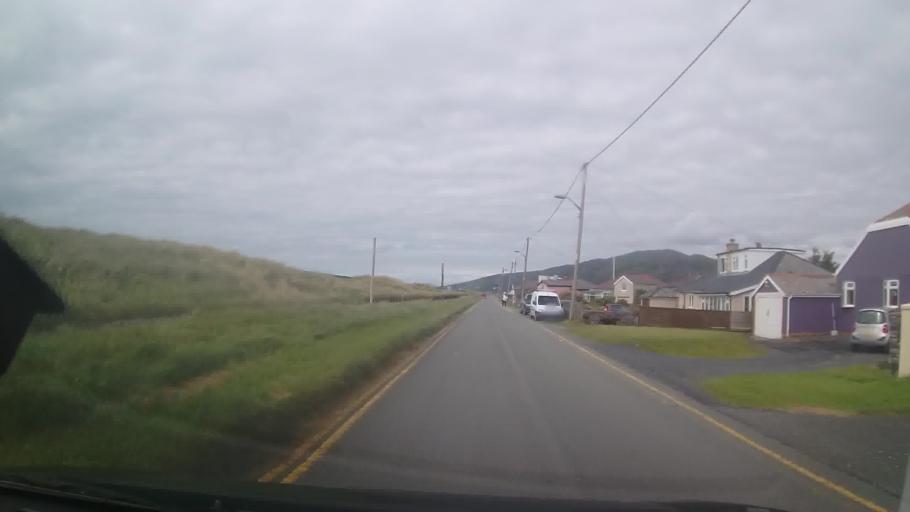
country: GB
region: Wales
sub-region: Gwynedd
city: Barmouth
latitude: 52.6997
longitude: -4.0572
